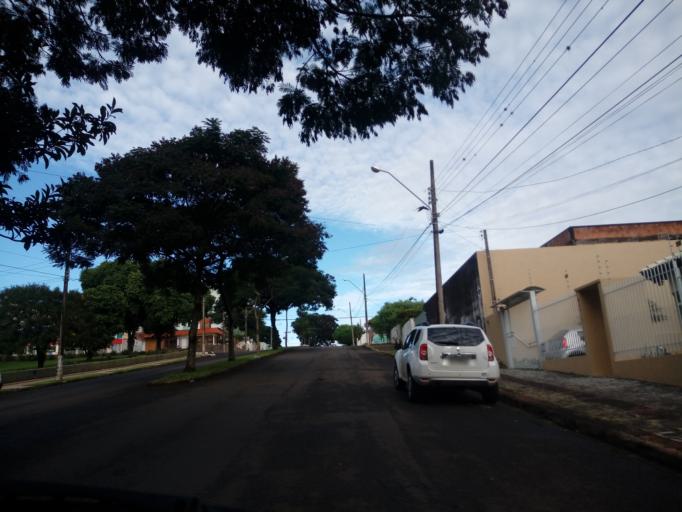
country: BR
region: Santa Catarina
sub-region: Chapeco
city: Chapeco
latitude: -27.1062
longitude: -52.6210
